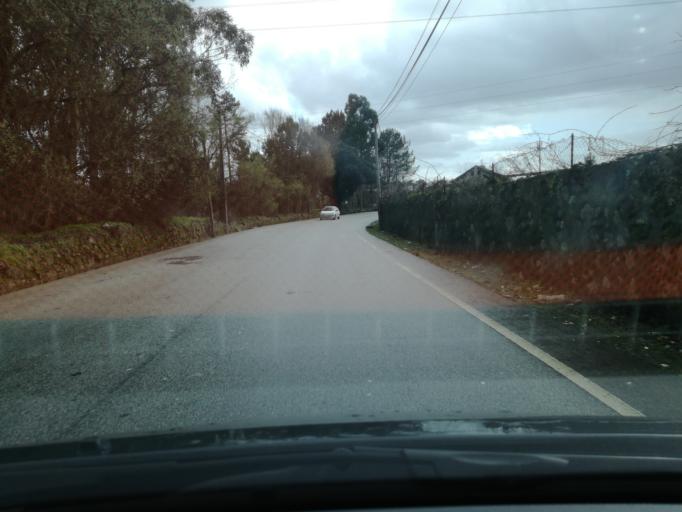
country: PT
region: Porto
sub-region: Valongo
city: Ermesinde
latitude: 41.2349
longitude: -8.5445
